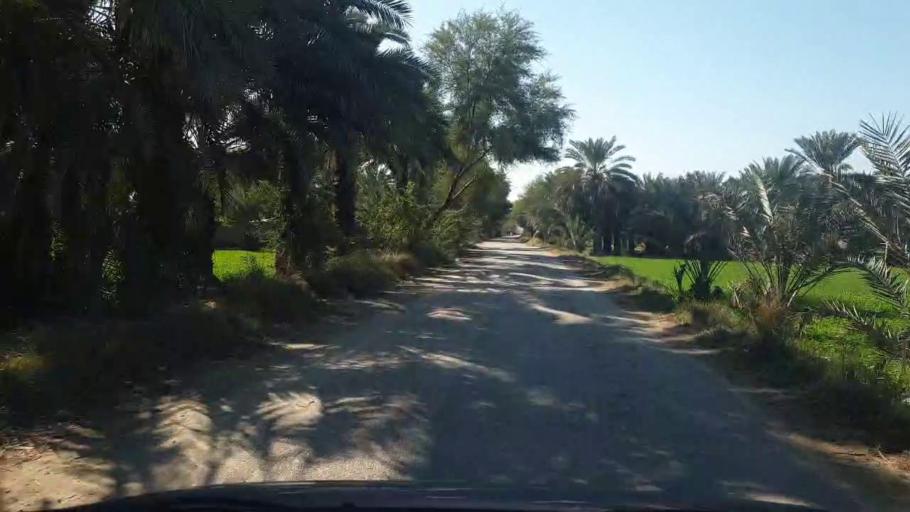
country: PK
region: Sindh
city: Bozdar
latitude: 27.1483
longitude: 68.6502
